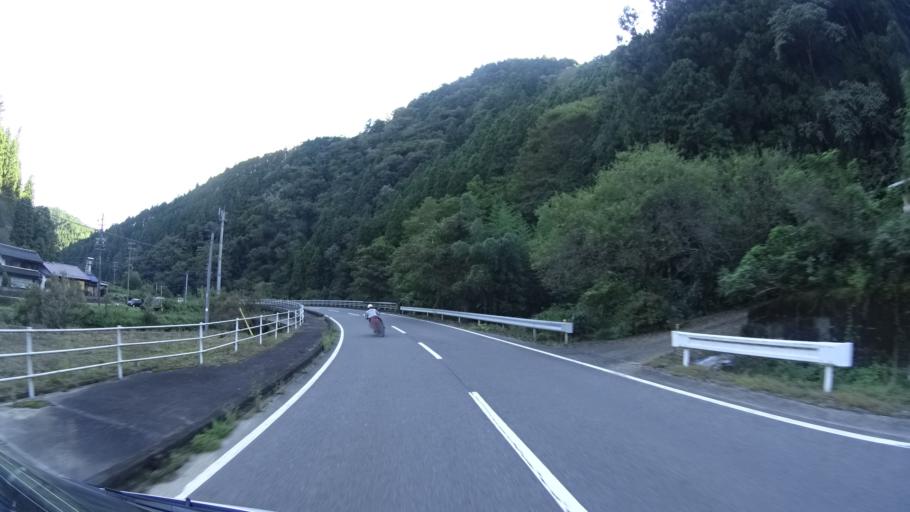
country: JP
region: Gifu
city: Minokamo
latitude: 35.5657
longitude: 137.1055
